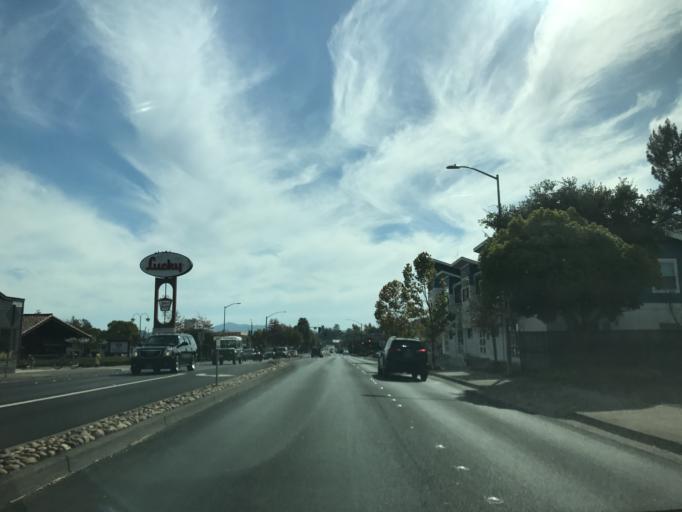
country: US
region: California
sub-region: Sonoma County
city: Petaluma
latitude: 38.2462
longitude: -122.6452
